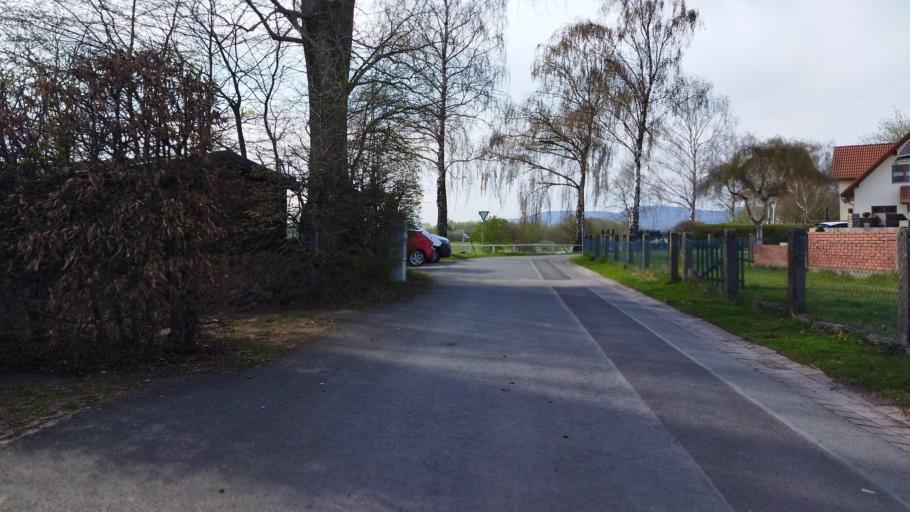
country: DE
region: Lower Saxony
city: Buchholz
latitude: 52.1792
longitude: 9.1606
